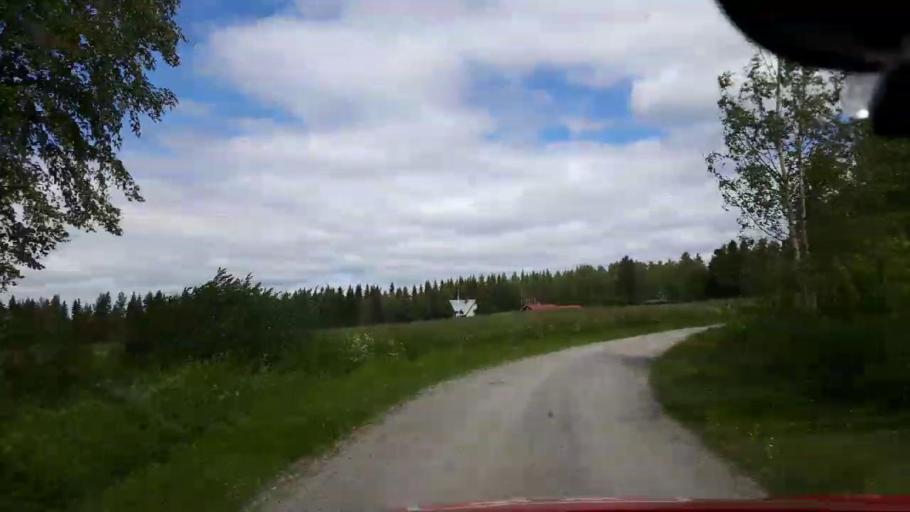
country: SE
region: Jaemtland
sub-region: Braecke Kommun
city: Braecke
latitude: 62.8298
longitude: 15.3059
